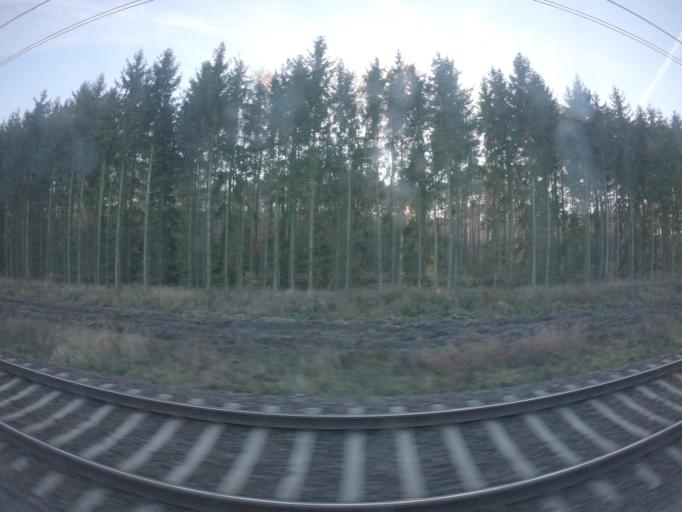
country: PL
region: Lubusz
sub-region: Powiat slubicki
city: Rzepin
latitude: 52.2700
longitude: 14.9270
